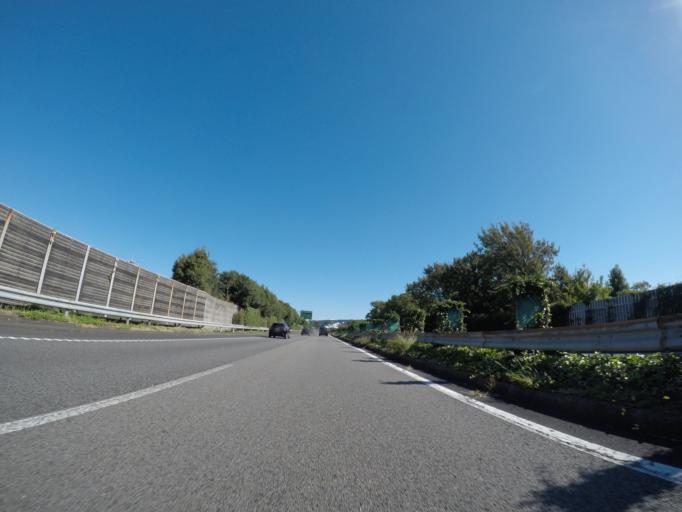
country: JP
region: Shizuoka
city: Shizuoka-shi
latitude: 34.9560
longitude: 138.4135
